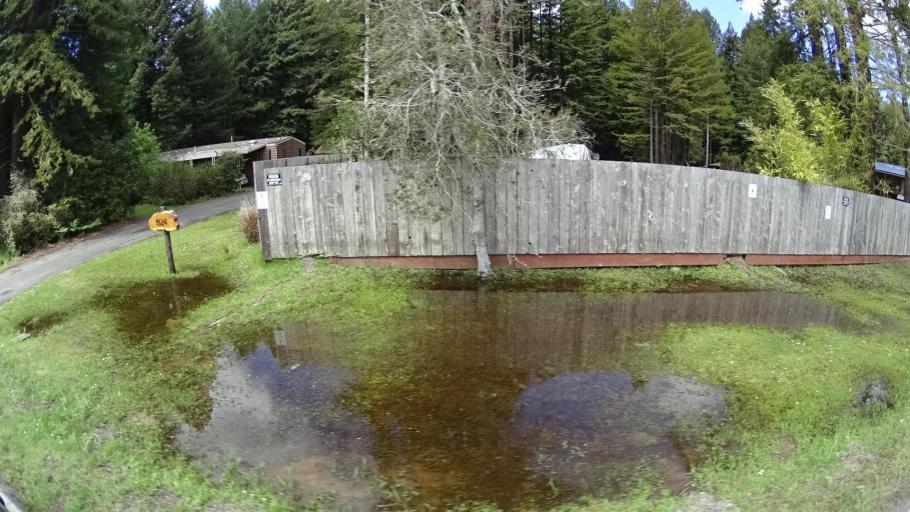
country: US
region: California
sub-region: Humboldt County
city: Blue Lake
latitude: 40.9227
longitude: -124.0221
